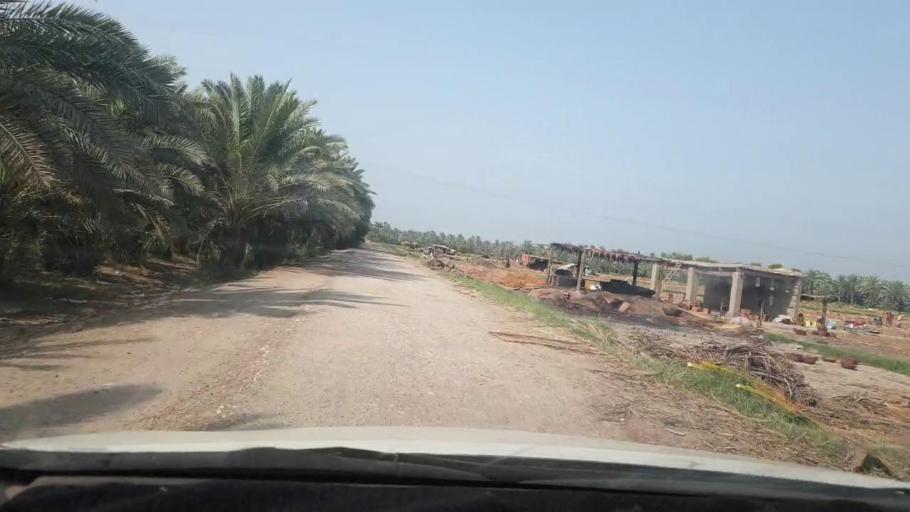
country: PK
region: Sindh
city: Rohri
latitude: 27.5976
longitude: 68.8682
